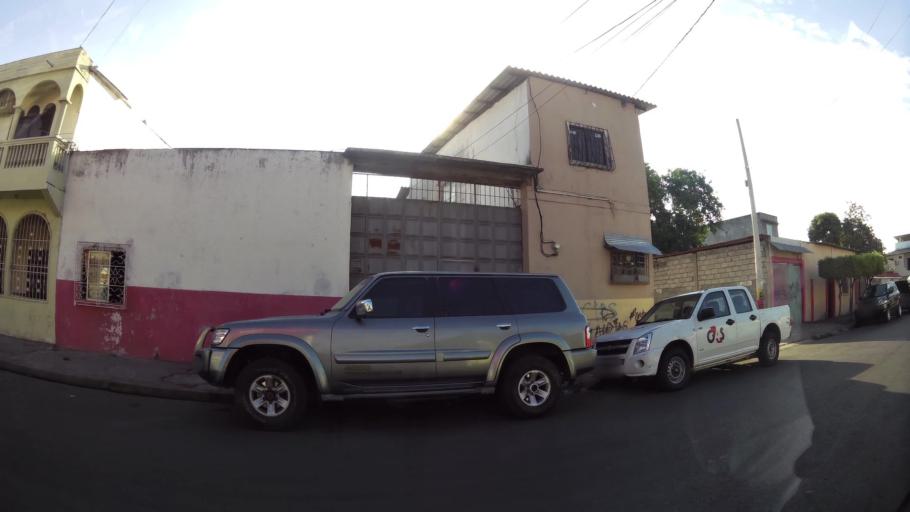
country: EC
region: Guayas
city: Guayaquil
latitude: -2.2256
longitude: -79.9059
